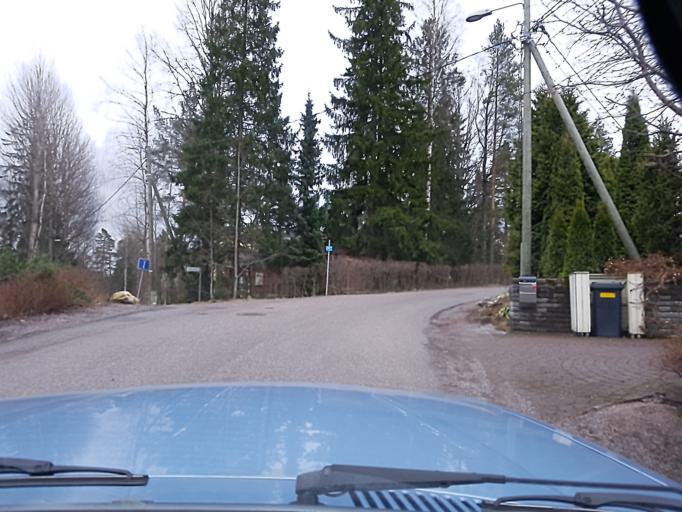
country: FI
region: Uusimaa
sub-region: Helsinki
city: Kauniainen
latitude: 60.2053
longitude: 24.7231
